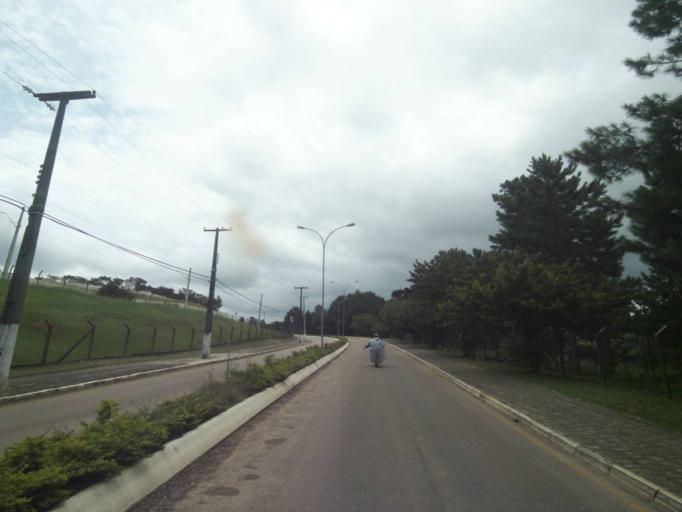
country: BR
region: Parana
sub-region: Campina Grande Do Sul
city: Campina Grande do Sul
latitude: -25.3065
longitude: -49.0582
